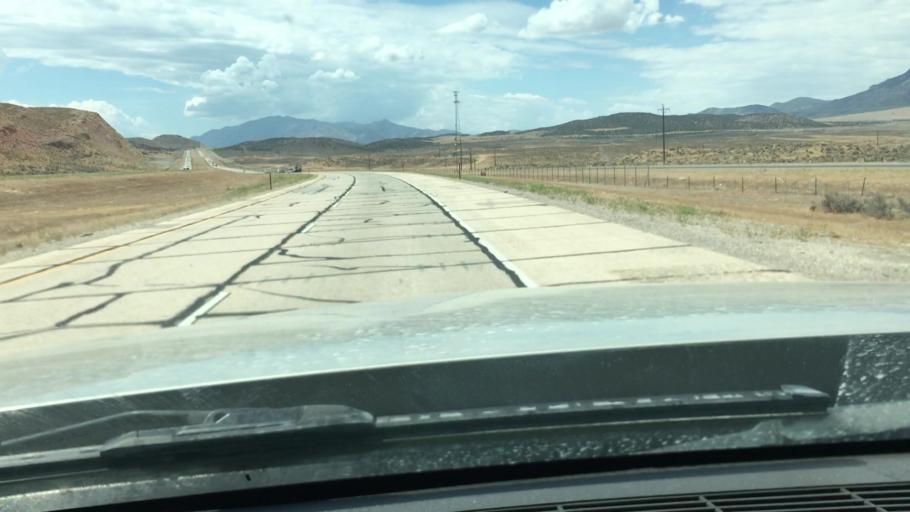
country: US
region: Utah
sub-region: Sanpete County
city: Gunnison
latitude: 39.3777
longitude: -112.0792
